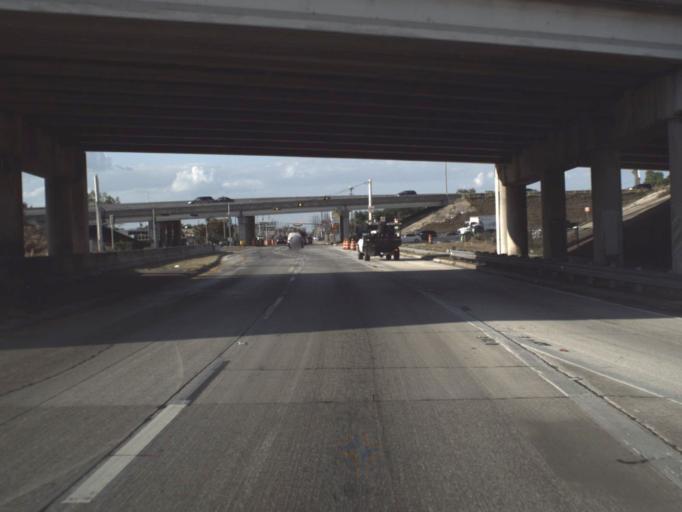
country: US
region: Florida
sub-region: Orange County
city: Holden Heights
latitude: 28.5099
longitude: -81.3969
